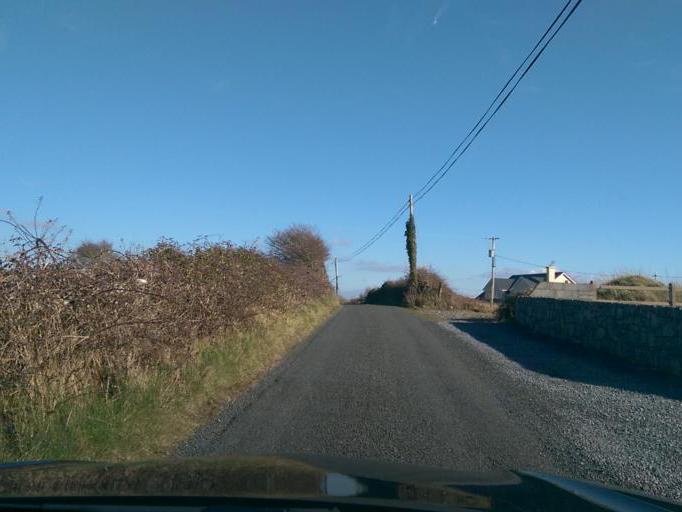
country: IE
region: Connaught
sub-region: County Galway
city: Oranmore
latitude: 53.2344
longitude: -8.9669
